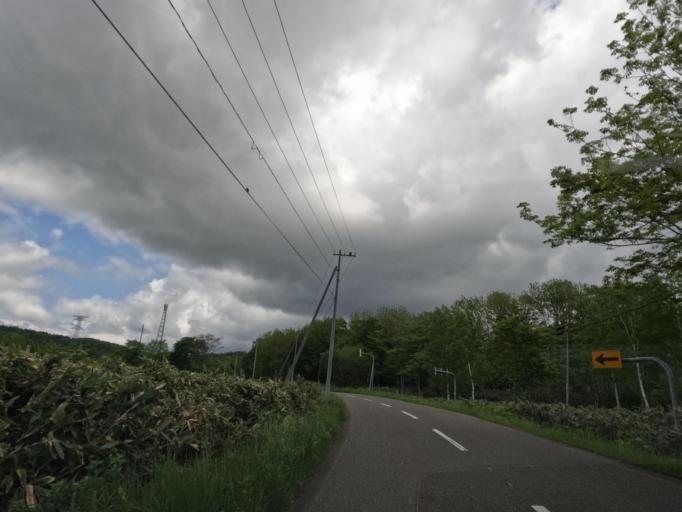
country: JP
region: Hokkaido
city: Tobetsu
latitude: 43.4626
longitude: 141.5975
